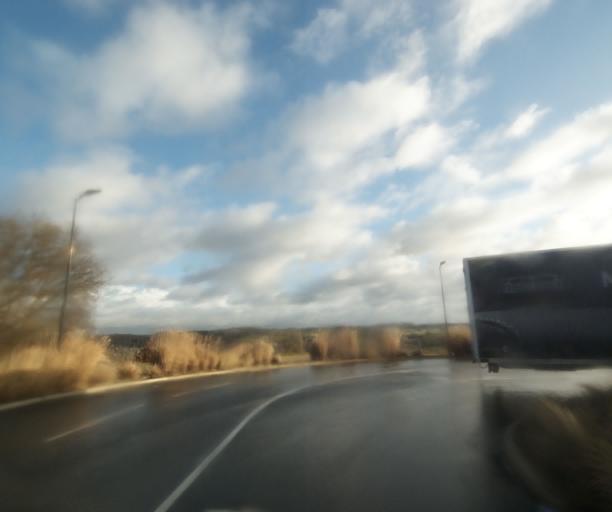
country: FR
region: Pays de la Loire
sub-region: Departement de la Sarthe
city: Coulaines
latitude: 48.0322
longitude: 0.1833
